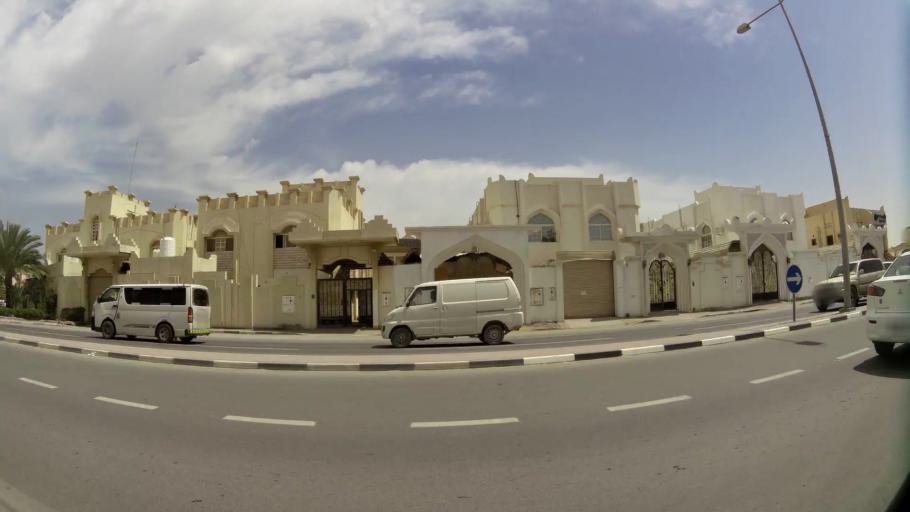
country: QA
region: Baladiyat ar Rayyan
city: Ar Rayyan
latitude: 25.2682
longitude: 51.4202
